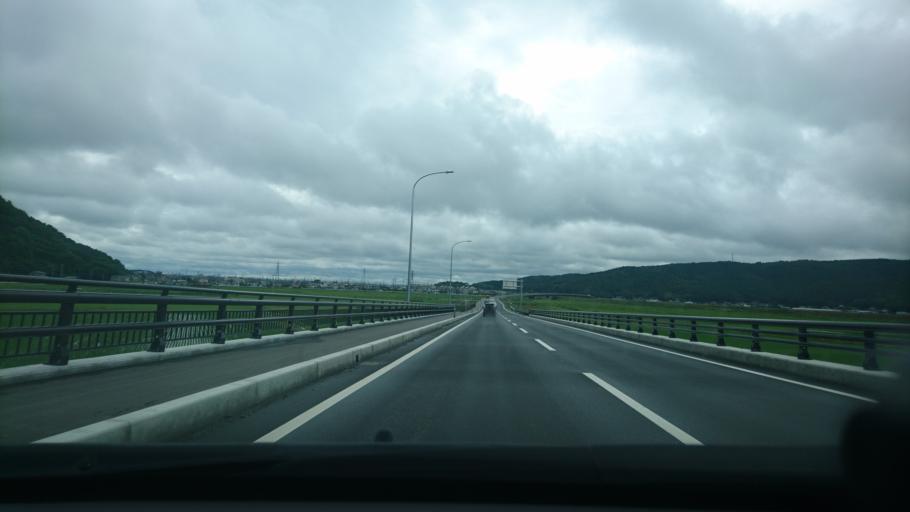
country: JP
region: Miyagi
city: Ishinomaki
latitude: 38.4486
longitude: 141.3466
